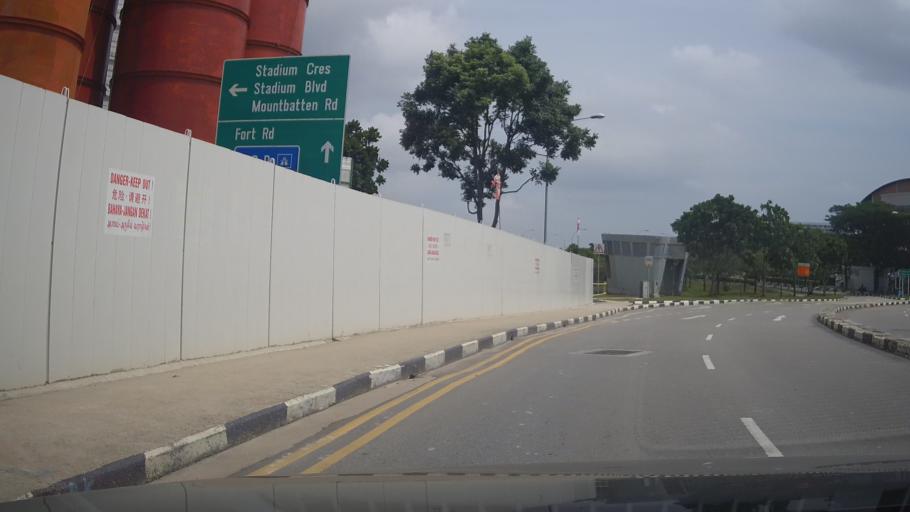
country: SG
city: Singapore
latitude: 1.2971
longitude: 103.8760
